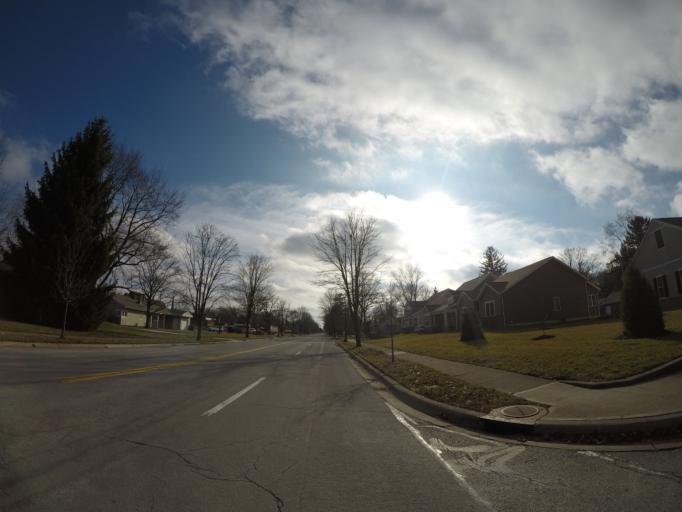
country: US
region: Ohio
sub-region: Franklin County
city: Upper Arlington
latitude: 40.0248
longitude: -83.0694
